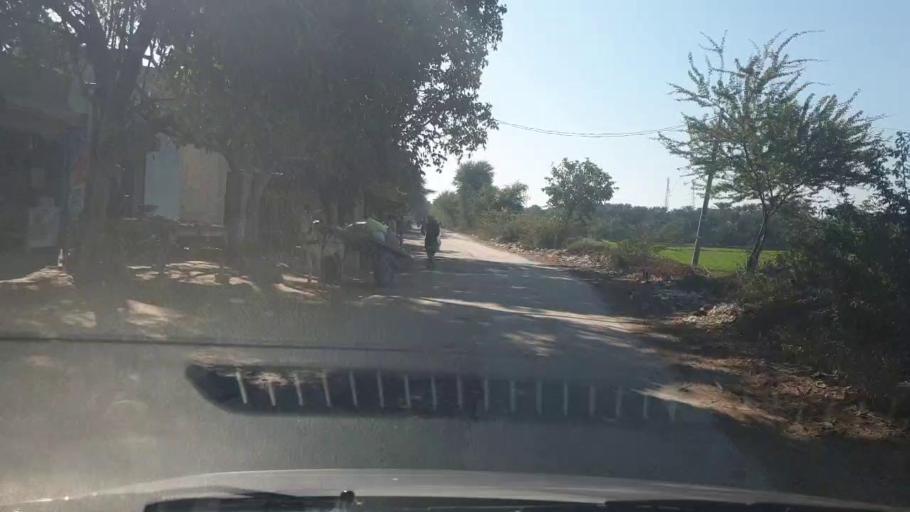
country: PK
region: Sindh
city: Bozdar
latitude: 27.1882
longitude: 68.6391
